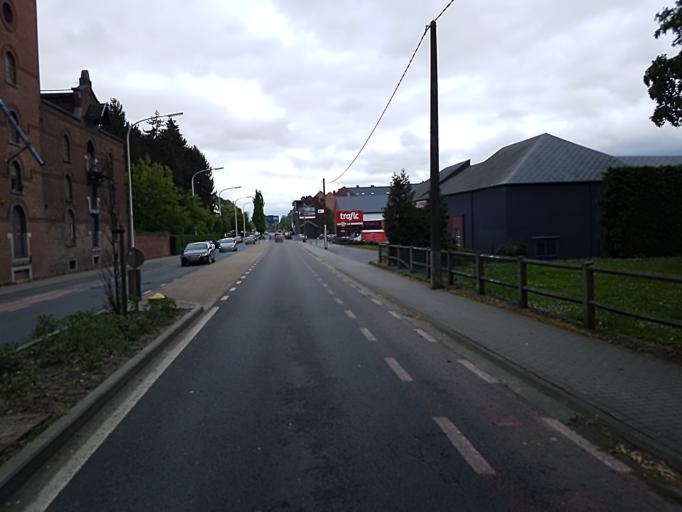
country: BE
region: Wallonia
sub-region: Province de Namur
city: Gembloux
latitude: 50.5655
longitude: 4.6891
